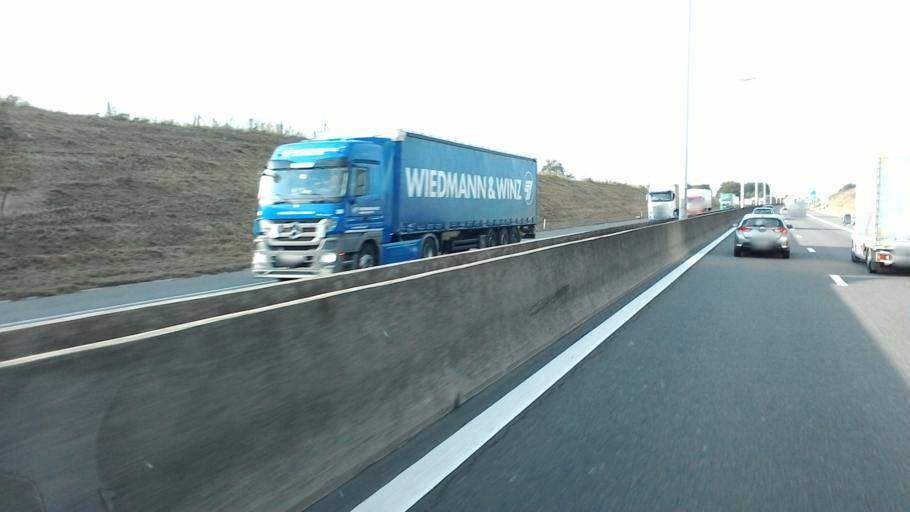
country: BE
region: Wallonia
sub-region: Province du Luxembourg
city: Leglise
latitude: 49.8386
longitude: 5.5114
